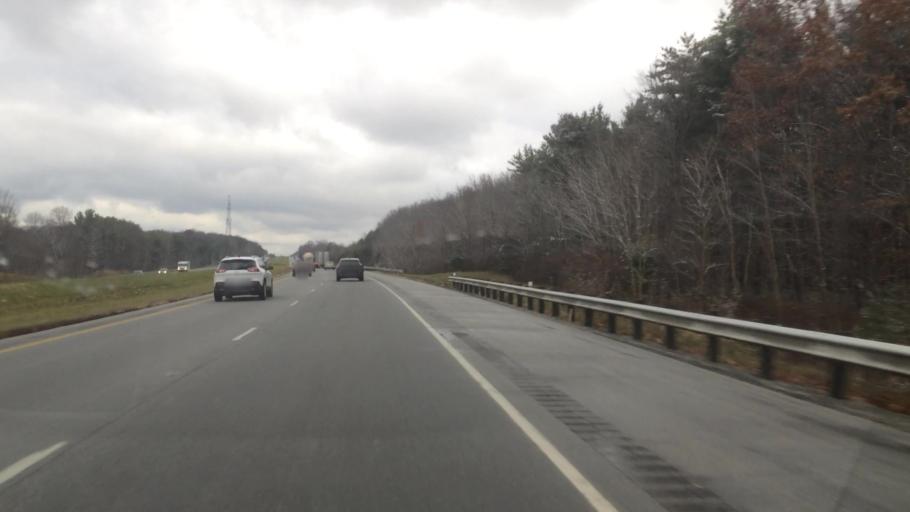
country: US
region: Ohio
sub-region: Summit County
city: Twinsburg
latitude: 41.2810
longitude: -81.4157
